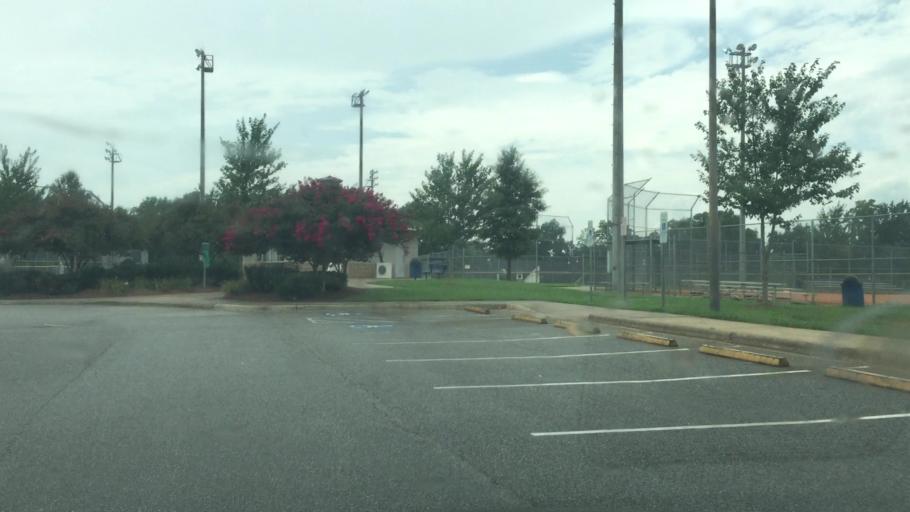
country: US
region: North Carolina
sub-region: Iredell County
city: Mooresville
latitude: 35.5963
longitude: -80.7844
